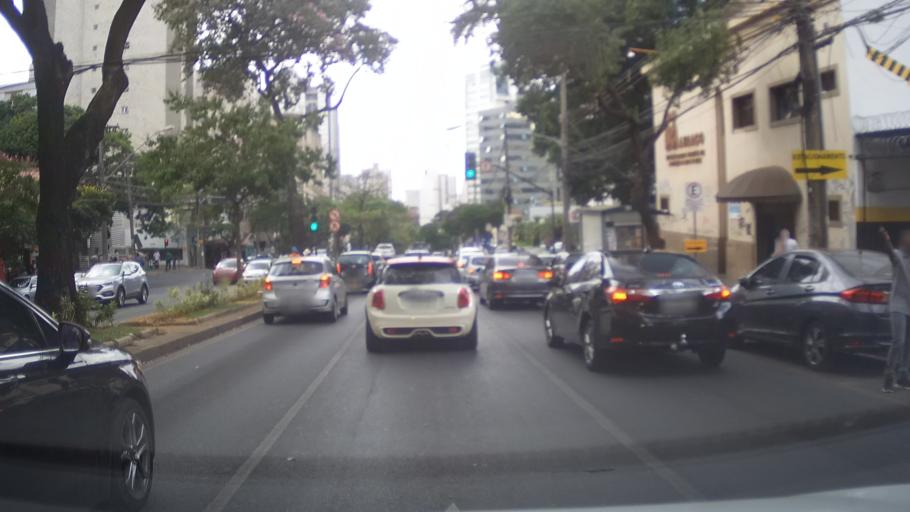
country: BR
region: Minas Gerais
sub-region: Belo Horizonte
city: Belo Horizonte
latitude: -19.9361
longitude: -43.9253
